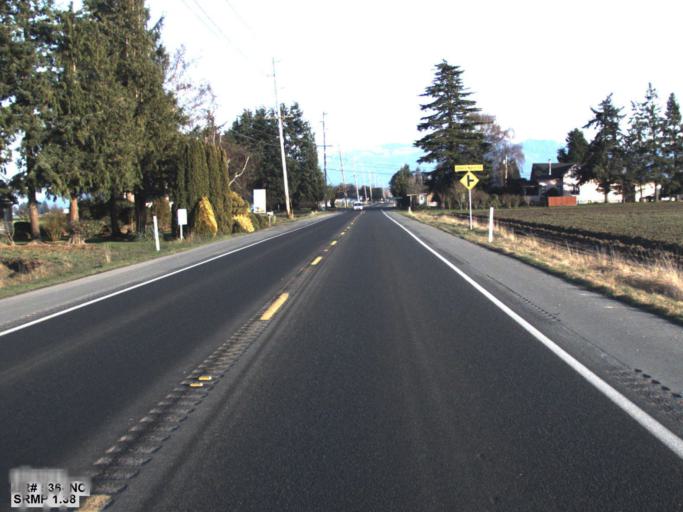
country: US
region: Washington
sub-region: Skagit County
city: Mount Vernon
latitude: 48.4428
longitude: -122.4031
